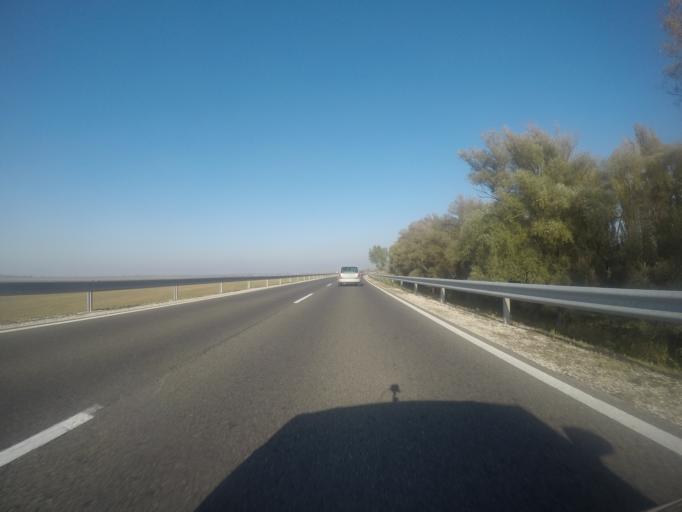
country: HU
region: Fejer
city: Ercsi
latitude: 47.2009
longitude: 18.8744
